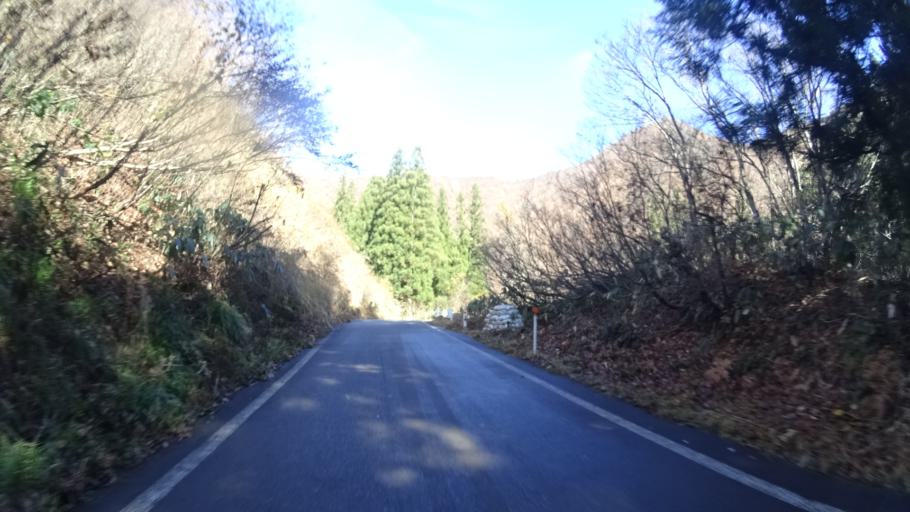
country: JP
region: Niigata
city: Muikamachi
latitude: 37.1774
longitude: 139.0867
